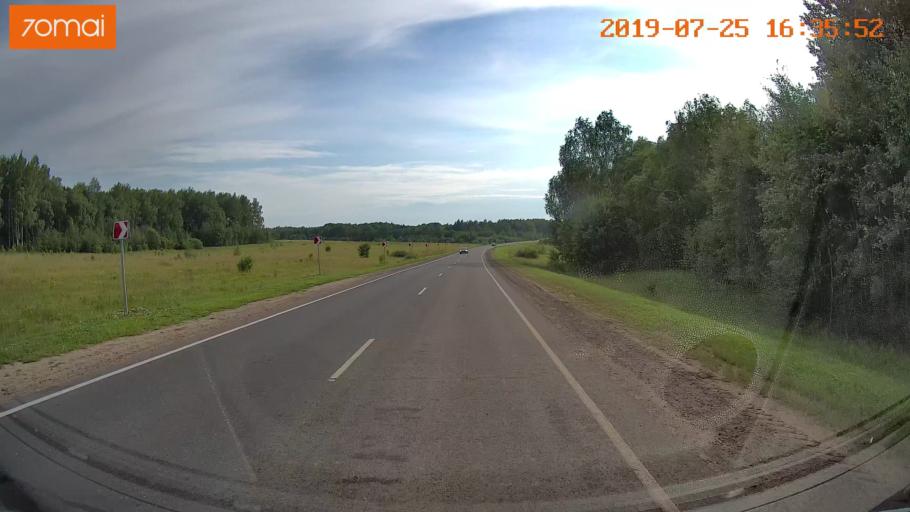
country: RU
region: Ivanovo
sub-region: Privolzhskiy Rayon
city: Ples
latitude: 57.4006
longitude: 41.4147
